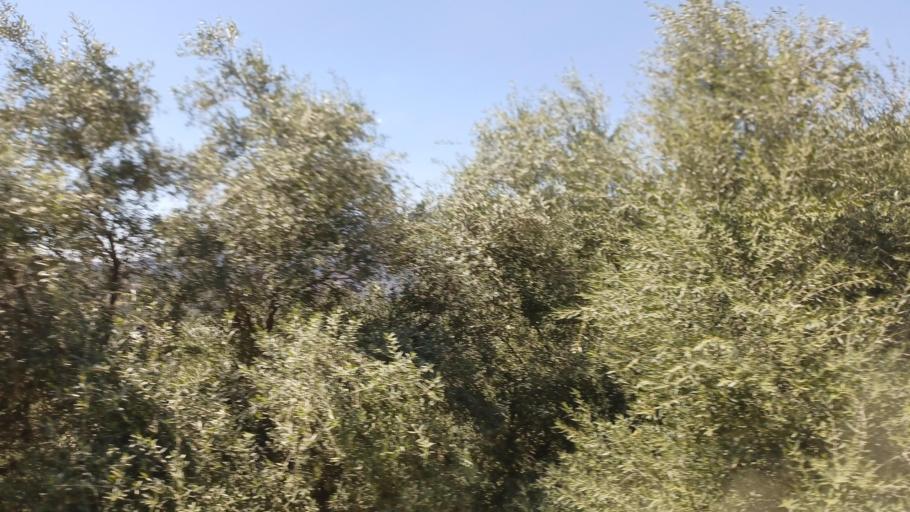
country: CY
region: Limassol
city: Parekklisha
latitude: 34.8173
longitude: 33.1455
